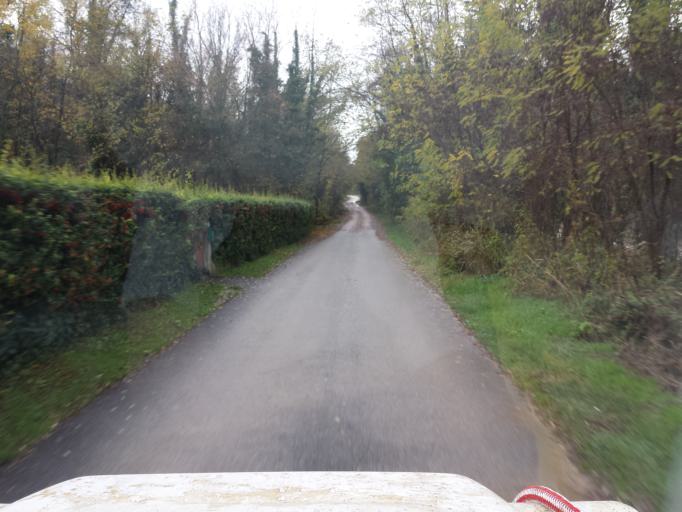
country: IT
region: Friuli Venezia Giulia
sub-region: Provincia di Gorizia
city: Medea
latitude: 45.9310
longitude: 13.4346
